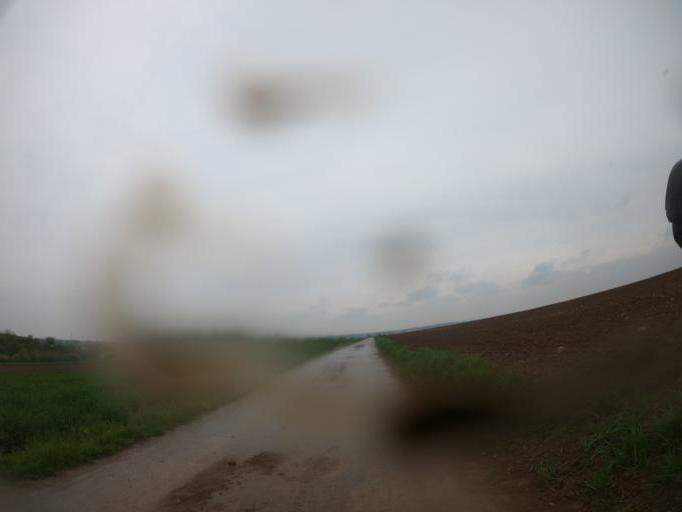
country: DE
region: Baden-Wuerttemberg
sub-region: Regierungsbezirk Stuttgart
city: Schwieberdingen
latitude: 48.8821
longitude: 9.0544
